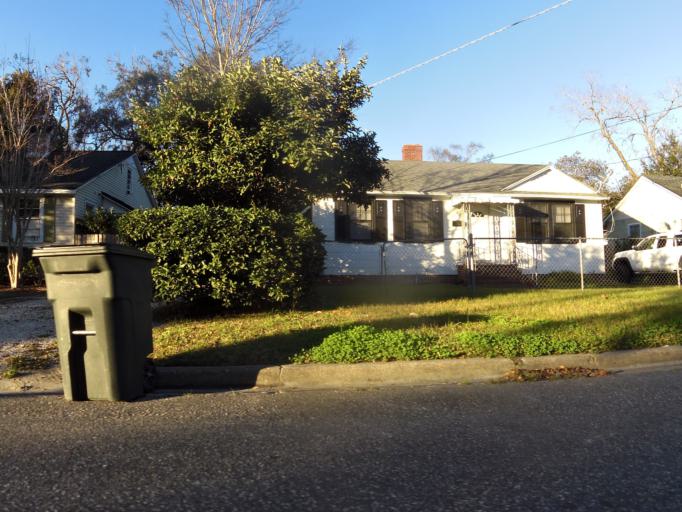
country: US
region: Florida
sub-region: Duval County
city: Jacksonville
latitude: 30.3176
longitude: -81.7150
